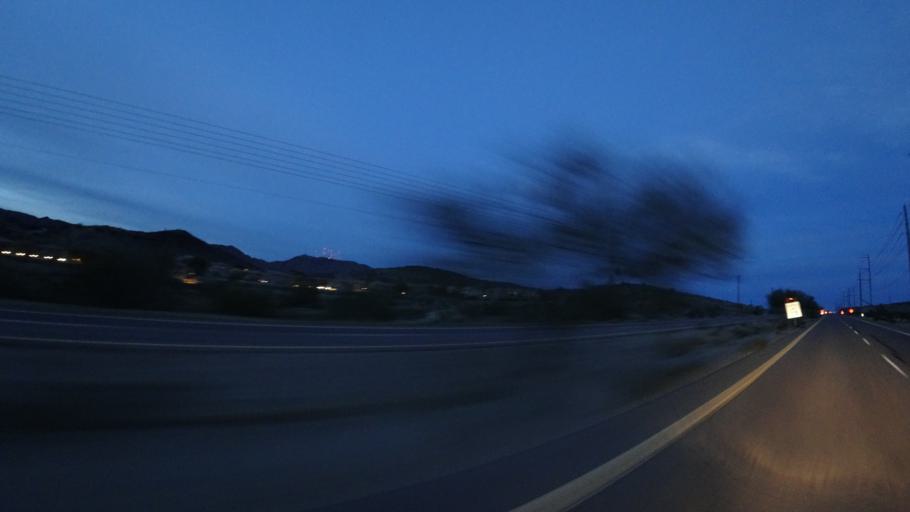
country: US
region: Arizona
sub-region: Maricopa County
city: Laveen
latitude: 33.2909
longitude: -112.0789
